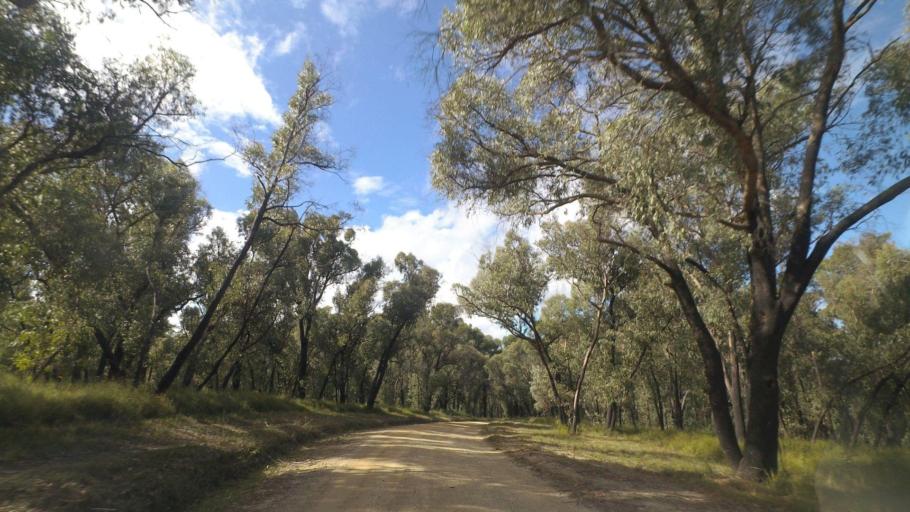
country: AU
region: Victoria
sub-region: Cardinia
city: Gembrook
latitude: -37.9868
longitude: 145.6393
